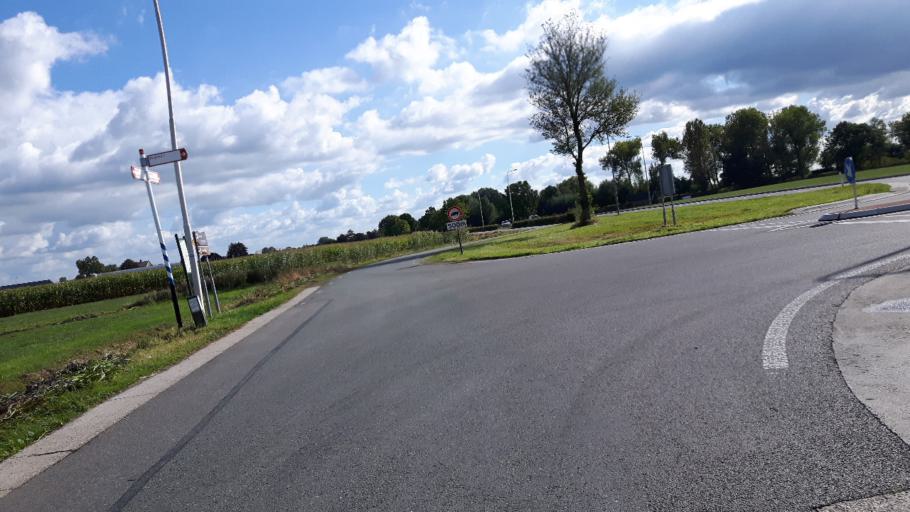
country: NL
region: South Holland
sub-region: Gemeente Leerdam
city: Leerdam
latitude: 51.8857
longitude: 5.1352
